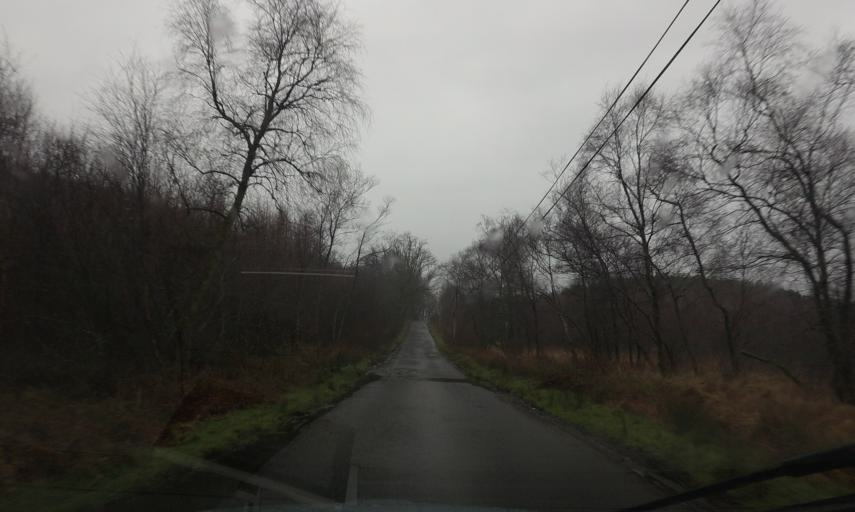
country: GB
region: Scotland
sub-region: West Dunbartonshire
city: Balloch
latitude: 56.1412
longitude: -4.6299
